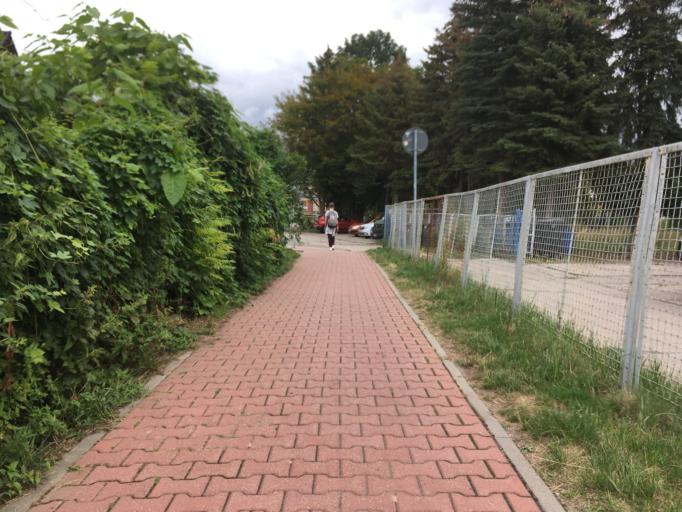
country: DE
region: Brandenburg
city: Prenzlau
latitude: 53.3087
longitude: 13.8477
